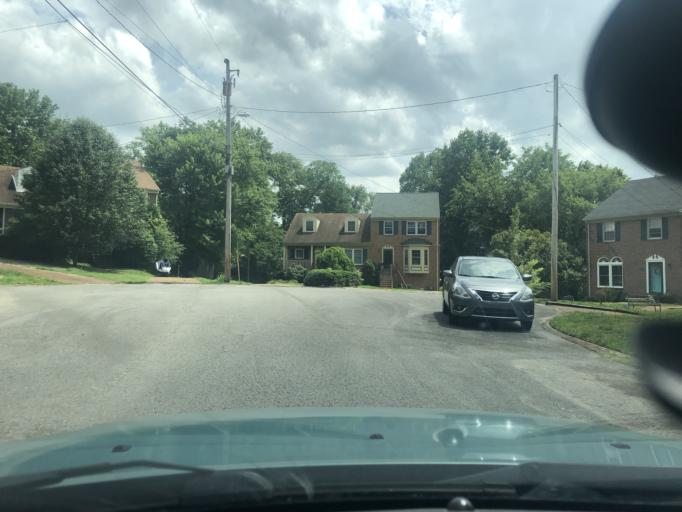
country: US
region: Tennessee
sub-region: Davidson County
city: Lakewood
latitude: 36.1297
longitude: -86.6362
